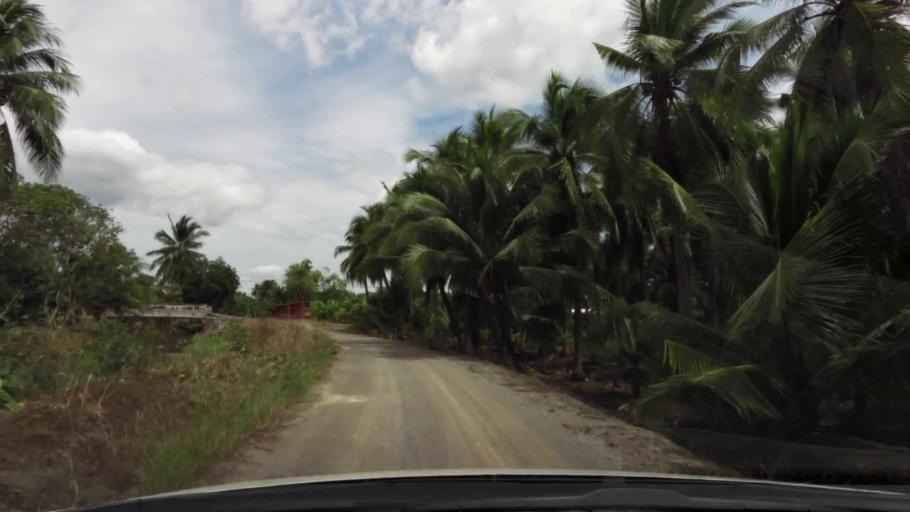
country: TH
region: Ratchaburi
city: Damnoen Saduak
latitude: 13.5106
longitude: 100.0066
